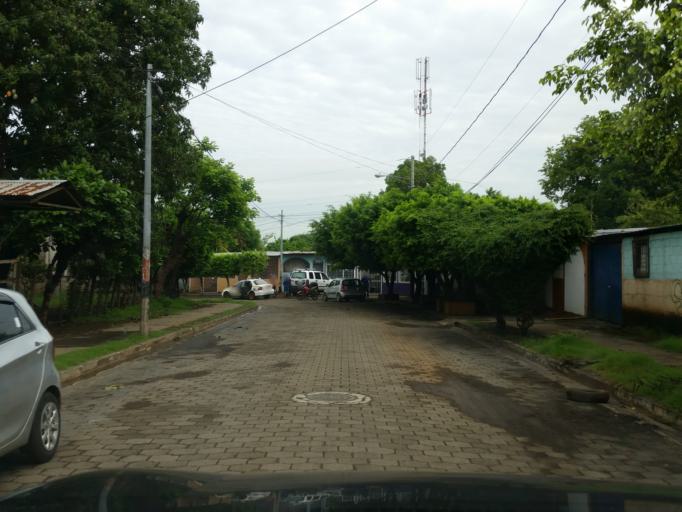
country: NI
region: Managua
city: Managua
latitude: 12.1032
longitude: -86.2206
